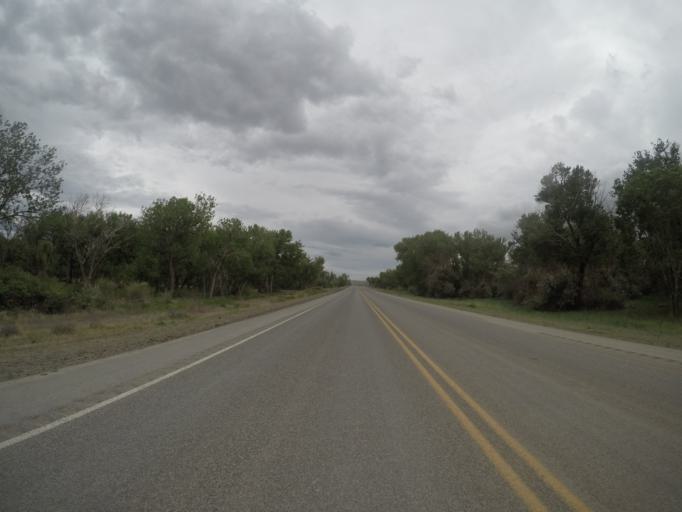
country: US
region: Wyoming
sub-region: Big Horn County
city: Lovell
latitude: 44.8619
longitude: -108.3316
